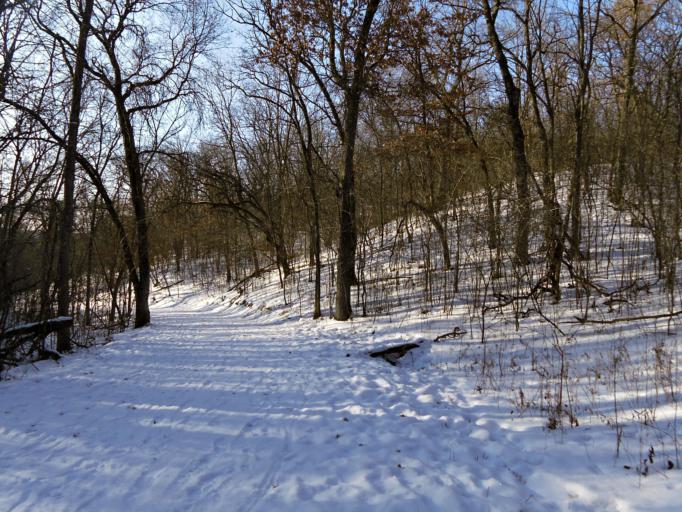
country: US
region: Wisconsin
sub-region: Saint Croix County
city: North Hudson
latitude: 45.0237
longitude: -92.6754
